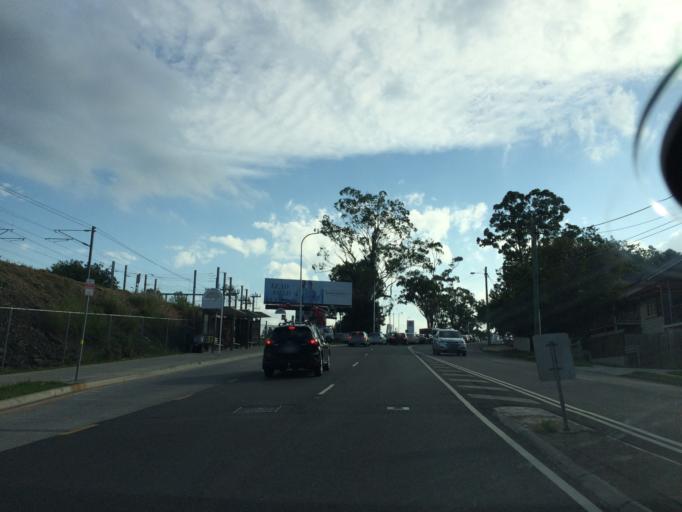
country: AU
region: Queensland
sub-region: Brisbane
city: Toowong
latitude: -27.4904
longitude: 152.9862
